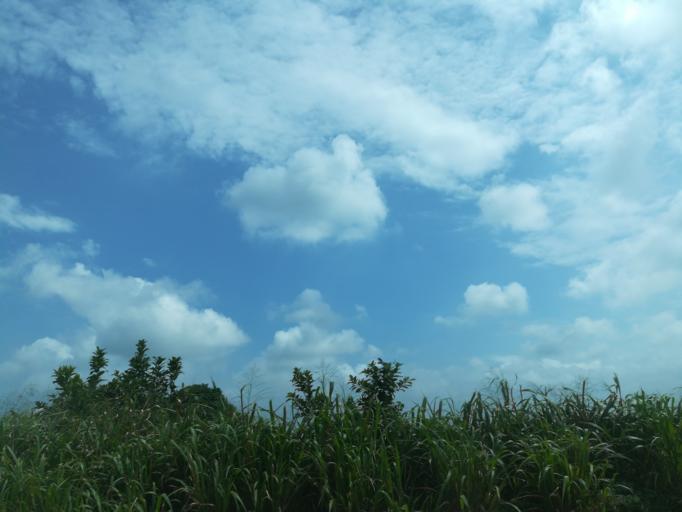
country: NG
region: Lagos
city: Ikorodu
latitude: 6.6529
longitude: 3.6994
